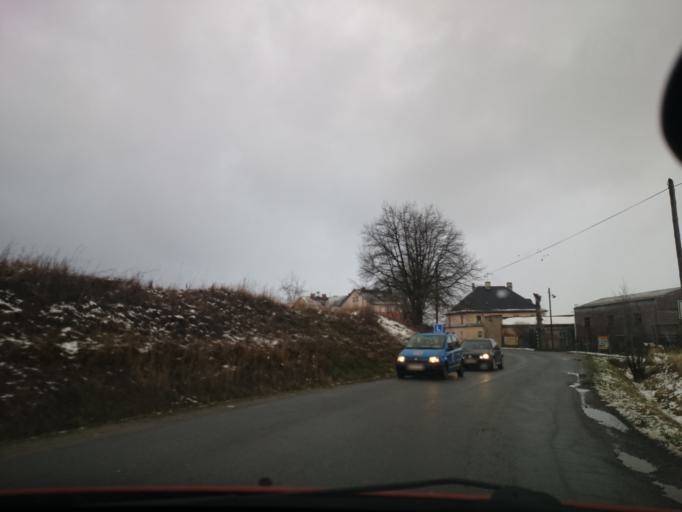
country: PL
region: Lower Silesian Voivodeship
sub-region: Powiat klodzki
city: Klodzko
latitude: 50.4162
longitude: 16.6399
